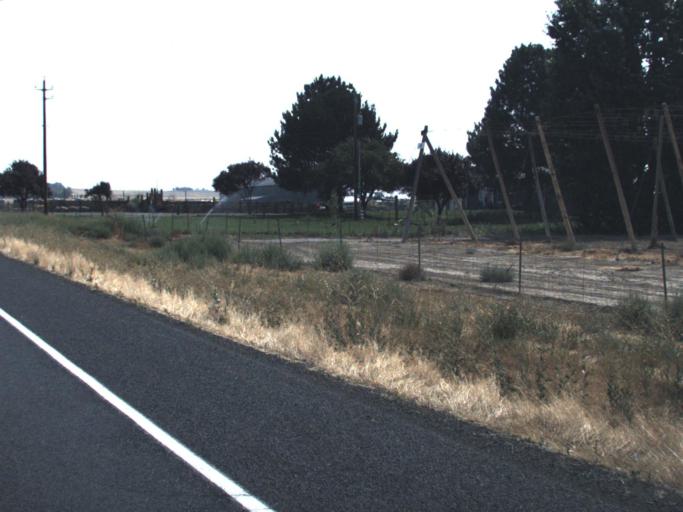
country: US
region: Washington
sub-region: Yakima County
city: Zillah
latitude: 46.5202
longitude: -120.2219
